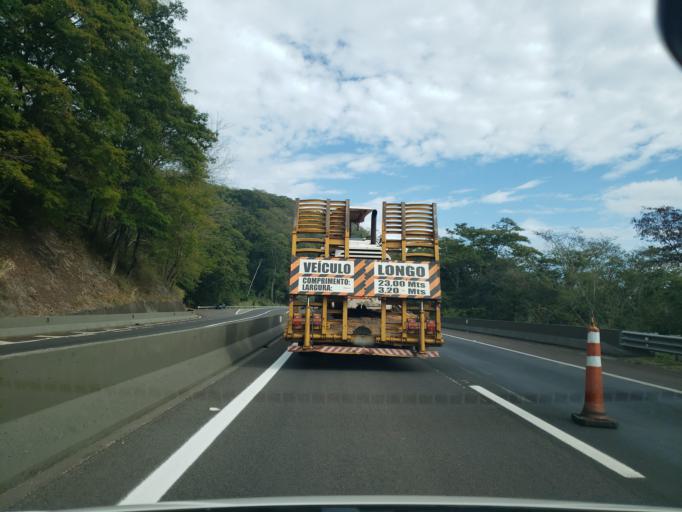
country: BR
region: Sao Paulo
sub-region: Dois Corregos
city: Dois Corregos
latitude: -22.2488
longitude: -48.3452
